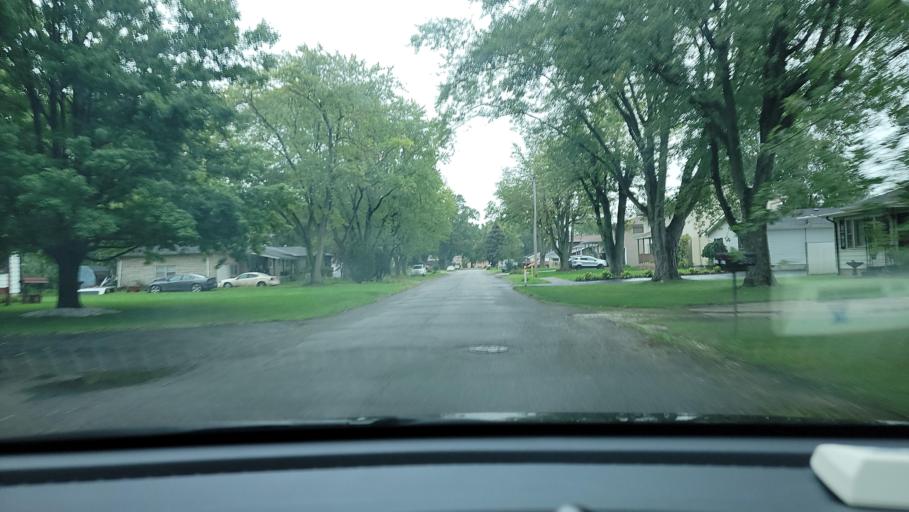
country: US
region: Indiana
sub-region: Porter County
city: Portage
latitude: 41.5709
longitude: -87.1813
